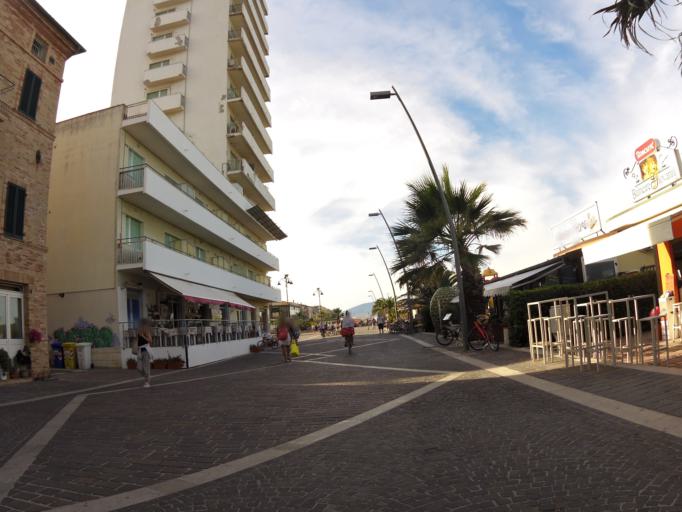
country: IT
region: The Marches
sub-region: Provincia di Macerata
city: Porto Recanati
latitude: 43.4351
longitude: 13.6643
